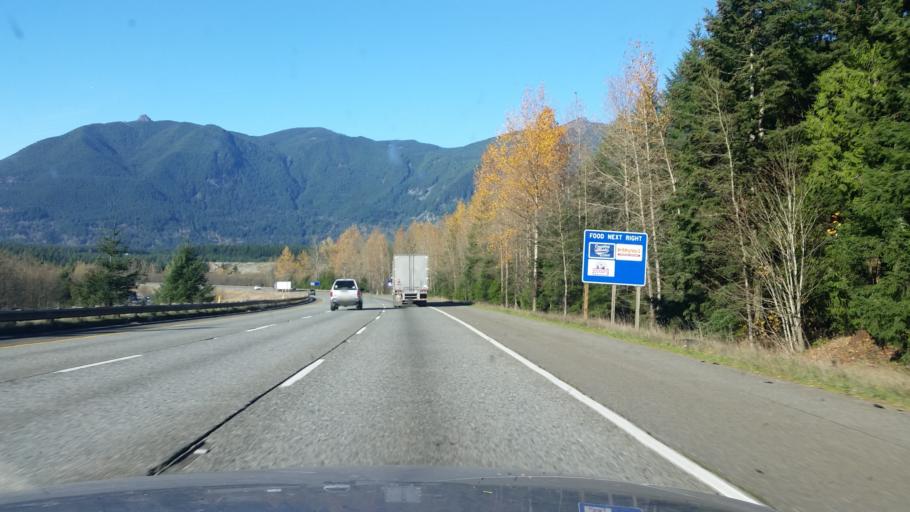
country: US
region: Washington
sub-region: King County
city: Tanner
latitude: 47.4574
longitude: -121.7023
